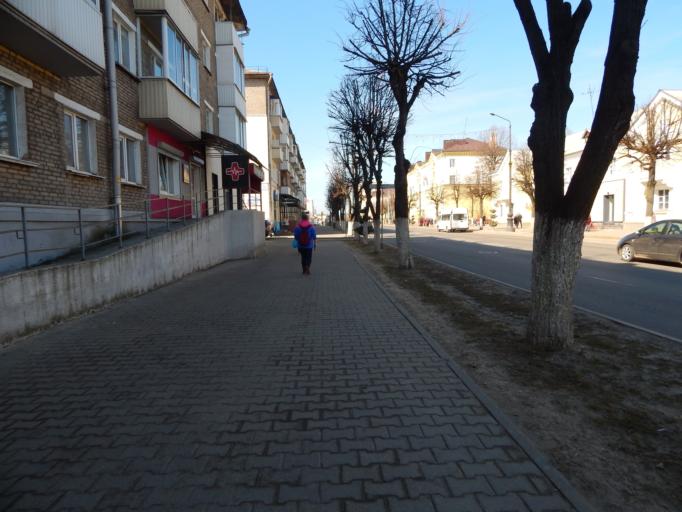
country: BY
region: Minsk
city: Horad Barysaw
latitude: 54.2236
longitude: 28.5146
